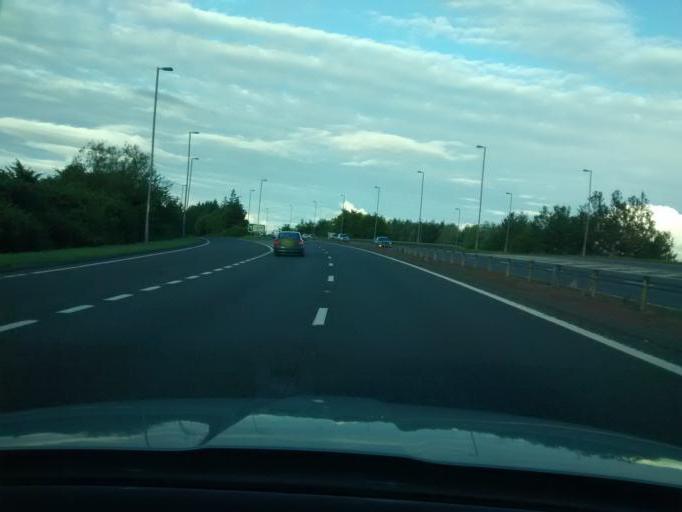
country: GB
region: Scotland
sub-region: Renfrewshire
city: Elderslie
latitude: 55.8445
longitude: -4.4867
